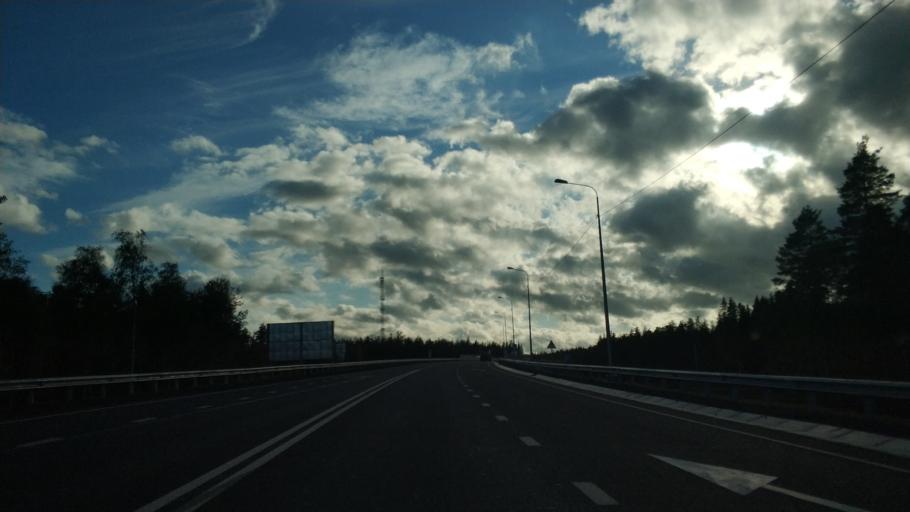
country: RU
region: Leningrad
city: Priozersk
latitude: 60.8456
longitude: 30.1406
